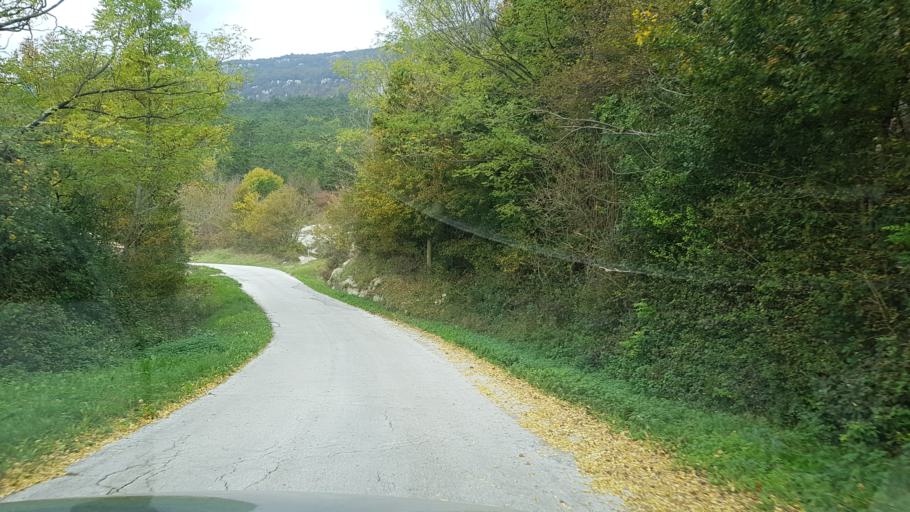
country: HR
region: Istarska
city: Buzet
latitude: 45.4080
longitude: 14.1186
